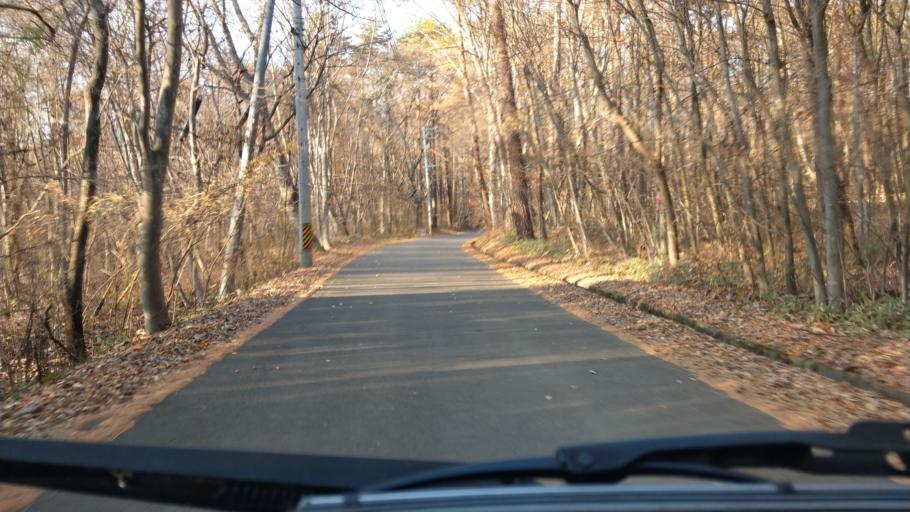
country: JP
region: Nagano
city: Komoro
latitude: 36.3557
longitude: 138.4551
